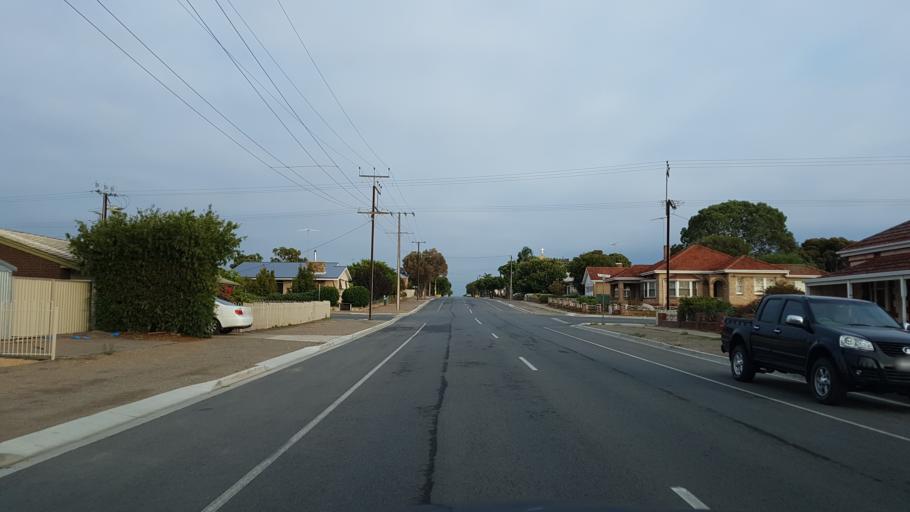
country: AU
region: South Australia
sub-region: Murray Bridge
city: Murray Bridge
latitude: -35.1215
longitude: 139.2678
